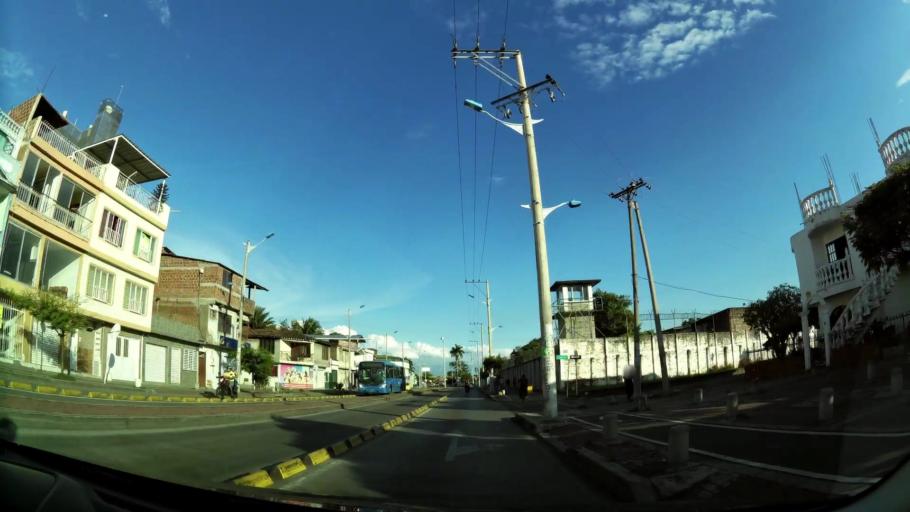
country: CO
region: Valle del Cauca
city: Cali
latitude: 3.4334
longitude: -76.5124
